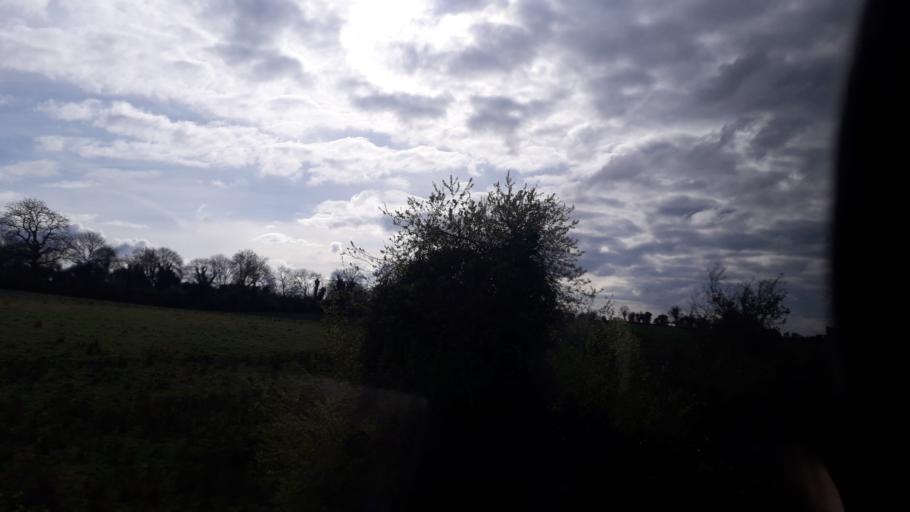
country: IE
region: Leinster
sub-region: An Iarmhi
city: An Muileann gCearr
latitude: 53.5040
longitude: -7.2778
